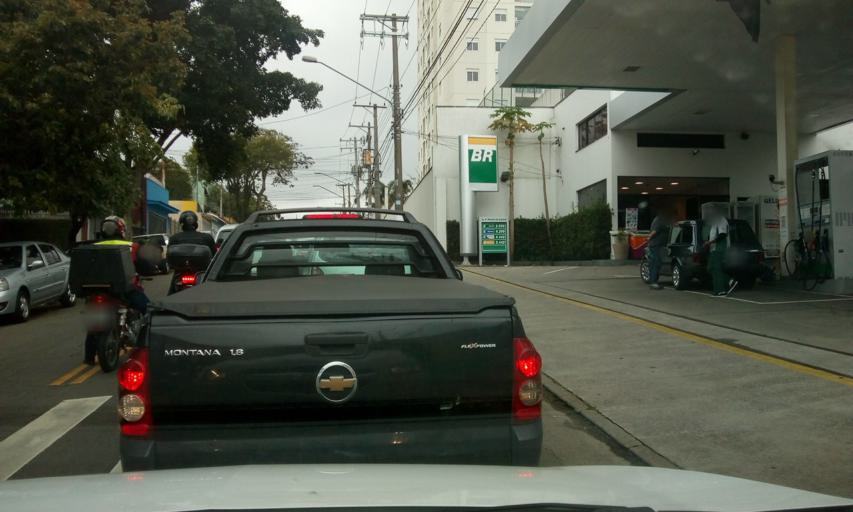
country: BR
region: Sao Paulo
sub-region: Sao Caetano Do Sul
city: Sao Caetano do Sul
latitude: -23.6213
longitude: -46.6049
